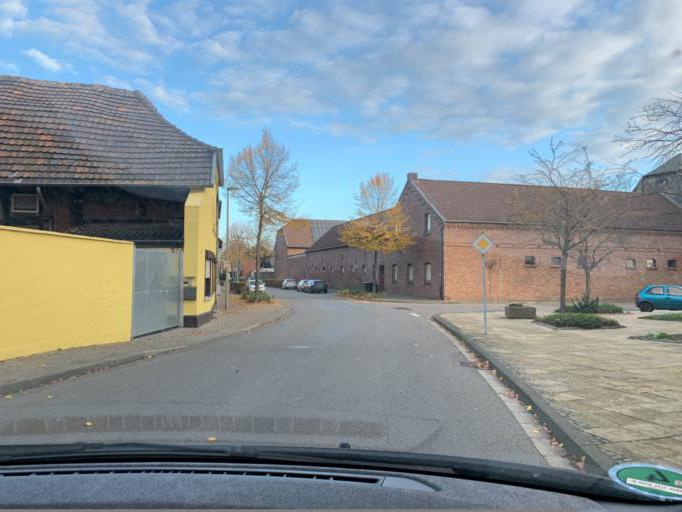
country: DE
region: North Rhine-Westphalia
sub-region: Regierungsbezirk Koln
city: Titz
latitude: 51.0480
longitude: 6.4046
